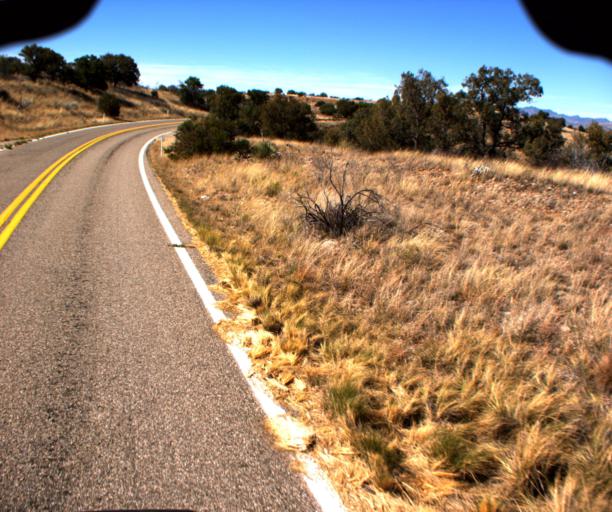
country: US
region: Arizona
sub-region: Cochise County
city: Sierra Vista
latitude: 31.5155
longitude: -110.4977
